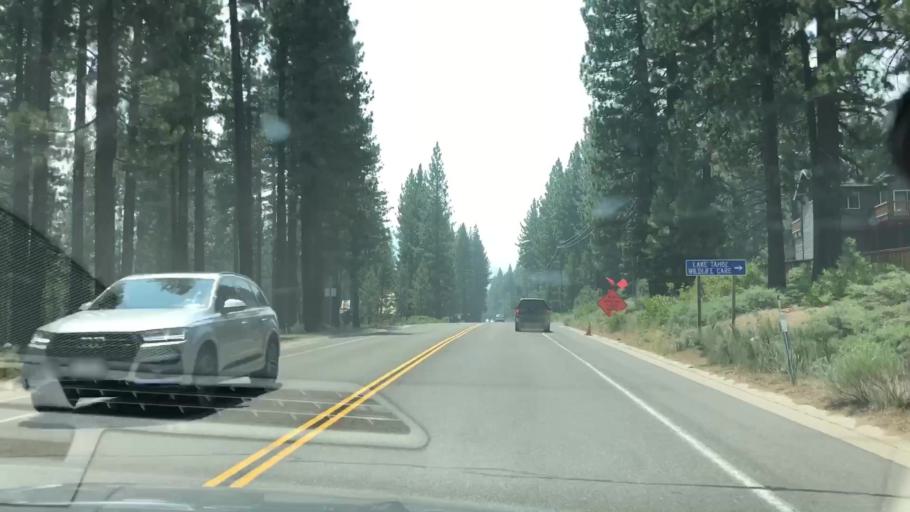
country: US
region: California
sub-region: El Dorado County
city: South Lake Tahoe
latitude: 38.8712
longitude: -119.9941
